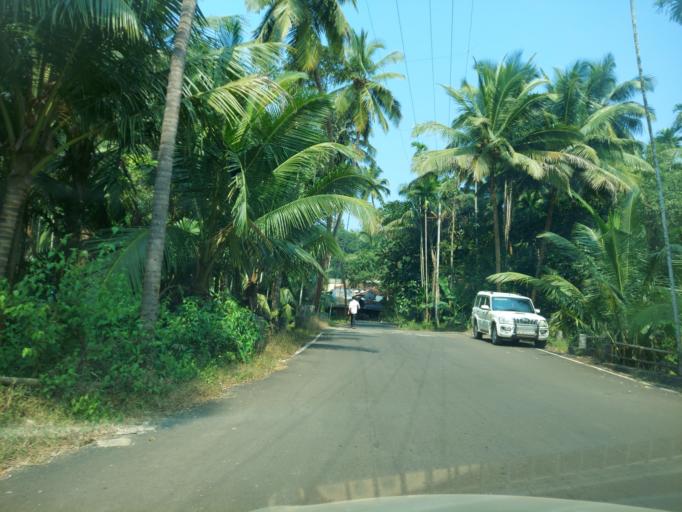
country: IN
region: Maharashtra
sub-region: Sindhudurg
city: Malvan
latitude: 15.9876
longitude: 73.5302
